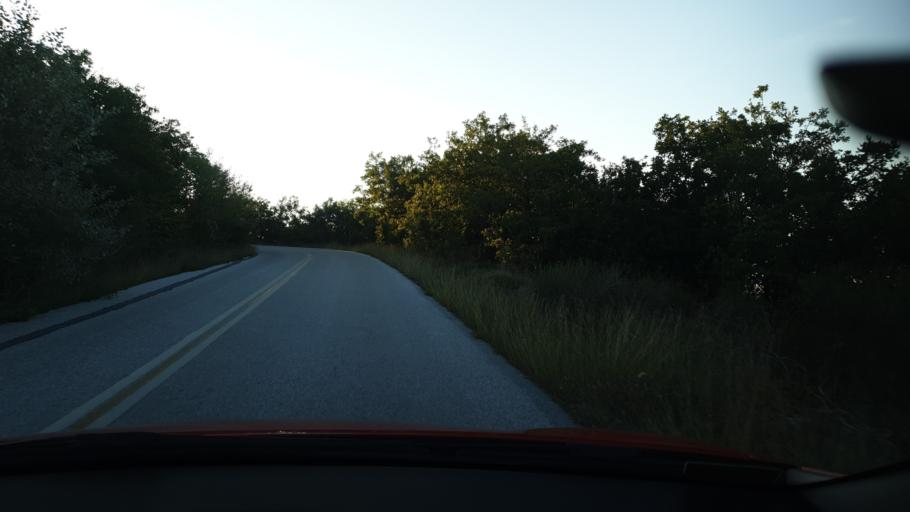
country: GR
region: Central Macedonia
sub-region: Nomos Chalkidikis
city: Galatista
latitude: 40.5188
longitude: 23.2731
